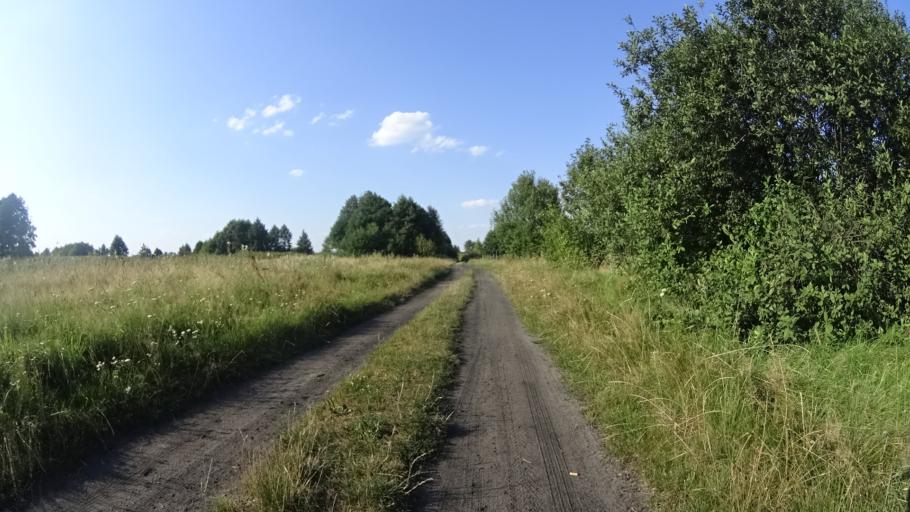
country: PL
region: Masovian Voivodeship
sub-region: Powiat bialobrzeski
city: Wysmierzyce
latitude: 51.6366
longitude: 20.8168
